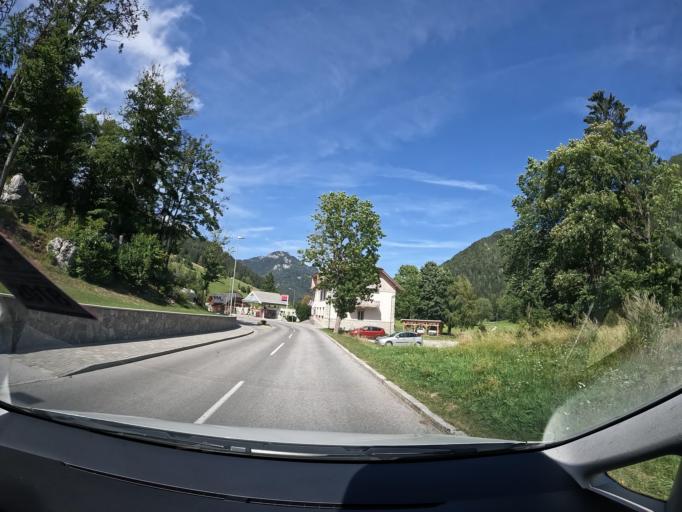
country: AT
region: Carinthia
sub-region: Politischer Bezirk Klagenfurt Land
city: Moosburg
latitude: 46.6756
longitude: 14.1237
